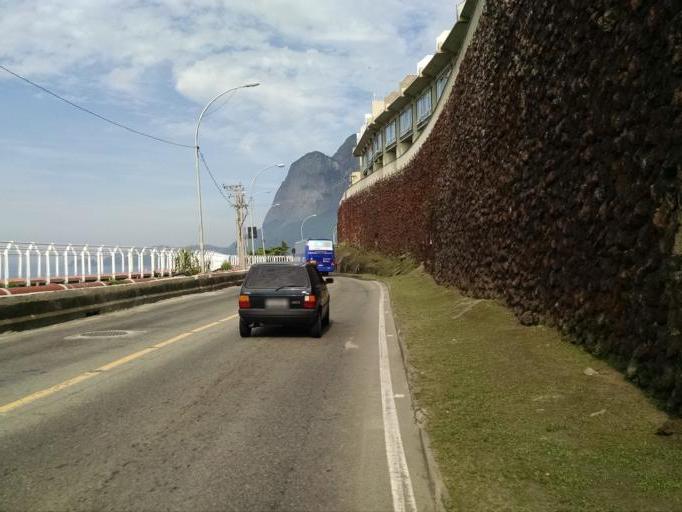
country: BR
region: Rio de Janeiro
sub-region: Rio De Janeiro
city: Rio de Janeiro
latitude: -23.0005
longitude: -43.2441
